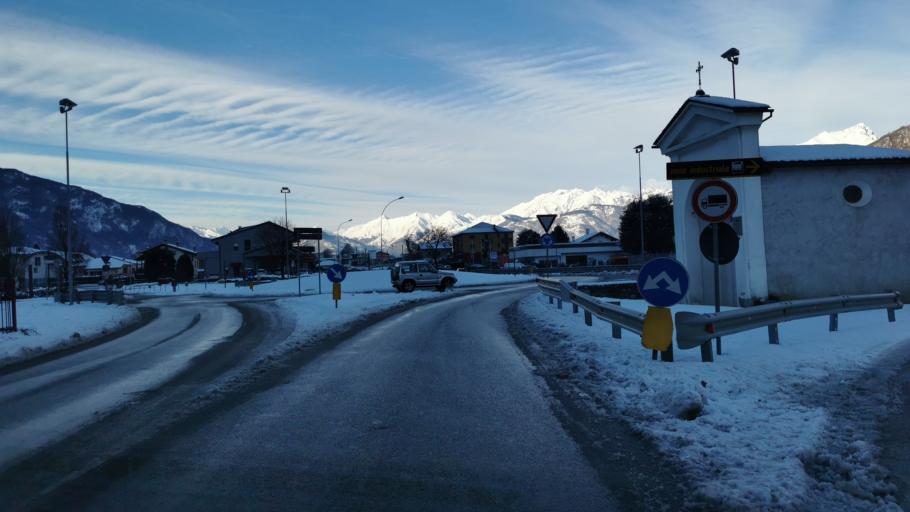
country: IT
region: Lombardy
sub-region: Provincia di Sondrio
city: Andalo Valtellino
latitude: 46.1371
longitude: 9.4781
